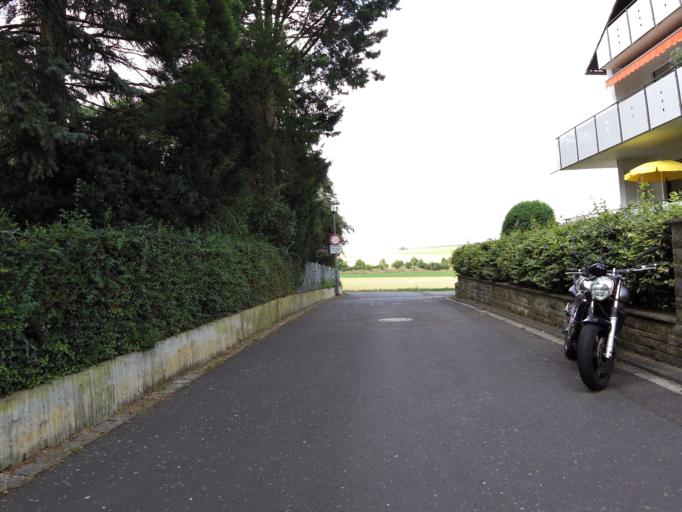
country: DE
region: Bavaria
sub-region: Regierungsbezirk Unterfranken
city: Estenfeld
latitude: 49.8338
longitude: 9.9985
